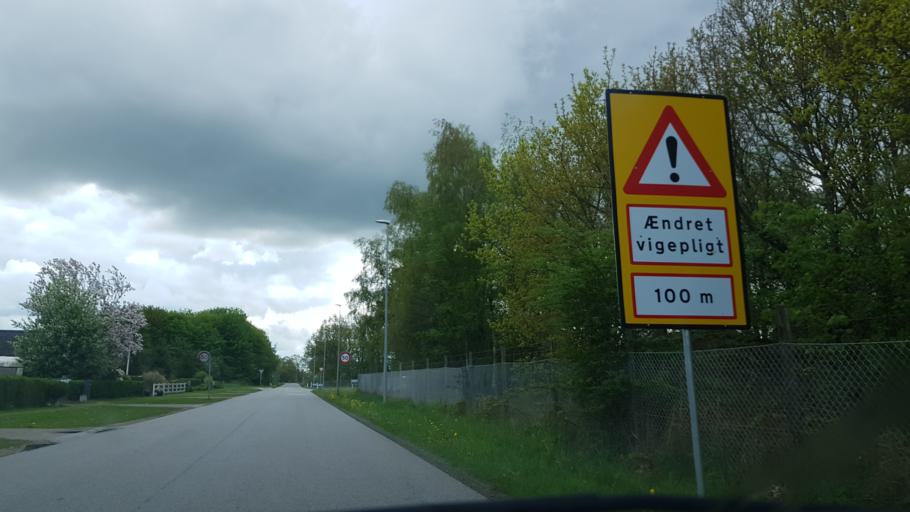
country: DK
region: South Denmark
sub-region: Haderslev Kommune
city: Vojens
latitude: 55.2404
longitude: 9.2625
